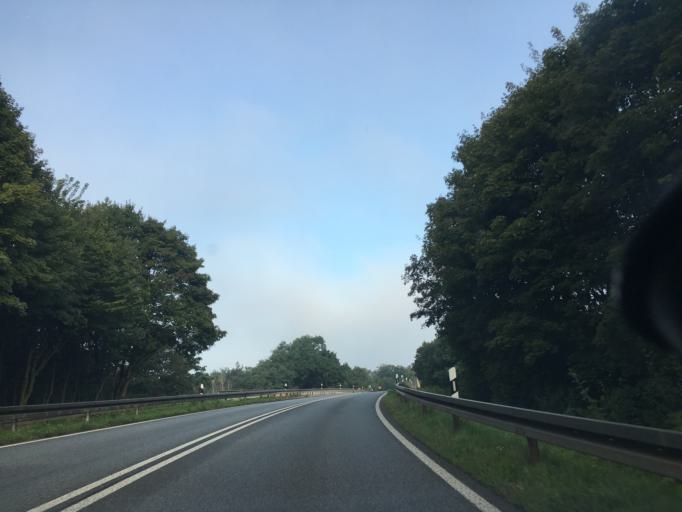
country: DE
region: Hesse
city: Niederrad
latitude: 50.0559
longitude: 8.6413
